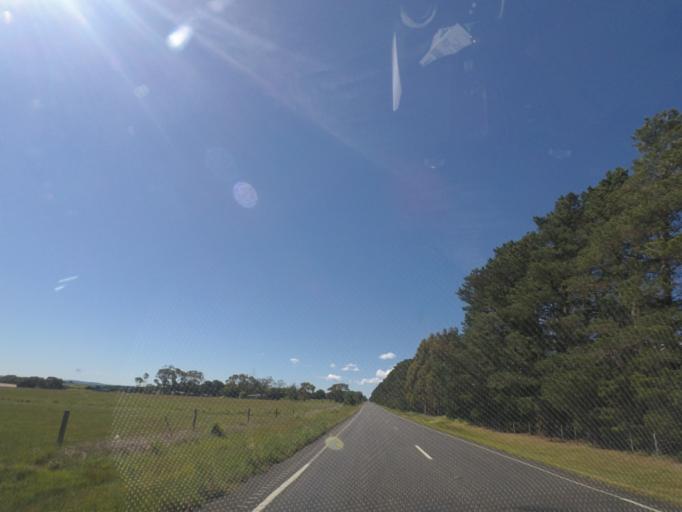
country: AU
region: Victoria
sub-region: Moorabool
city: Bacchus Marsh
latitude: -37.7673
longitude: 144.2180
